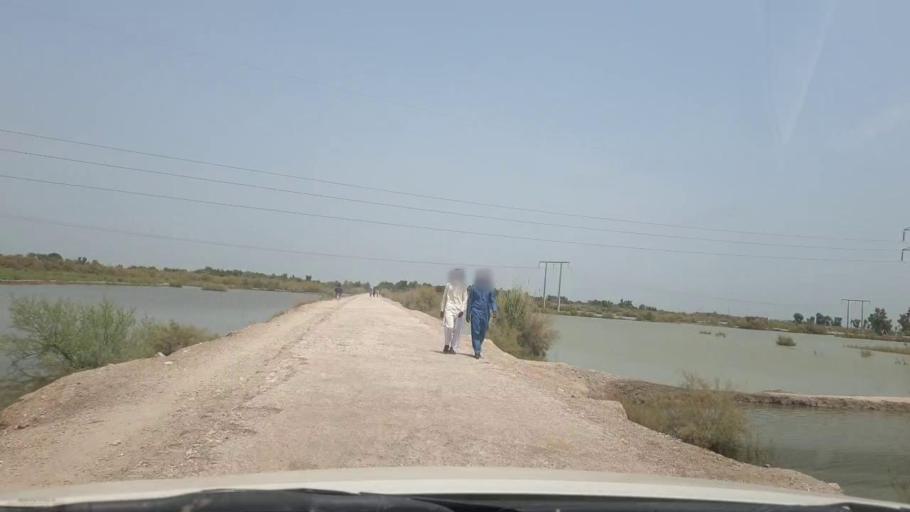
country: PK
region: Sindh
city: Rustam jo Goth
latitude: 28.0262
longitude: 68.8130
